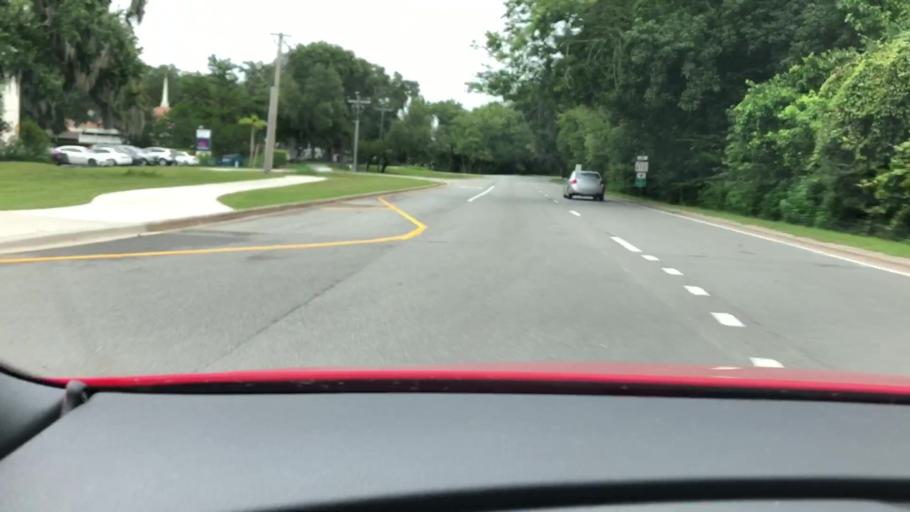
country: US
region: Florida
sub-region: Flagler County
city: Palm Coast
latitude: 29.5561
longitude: -81.2060
